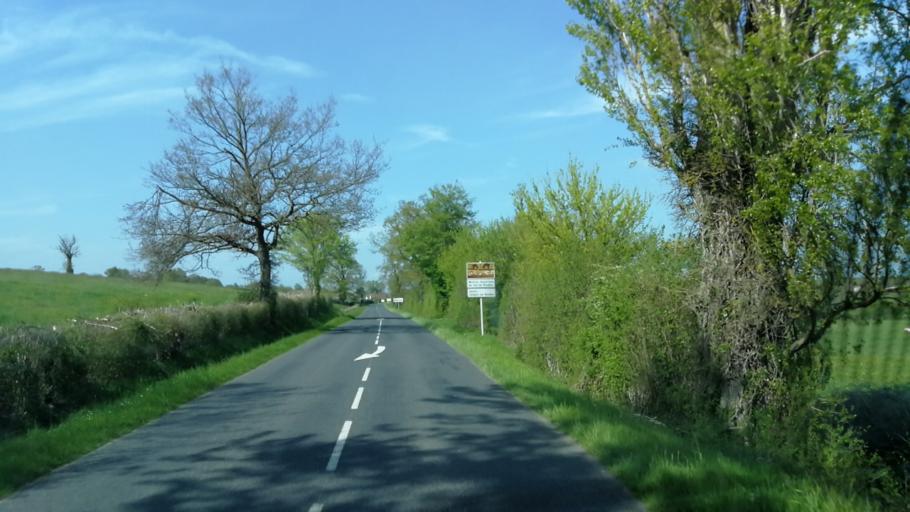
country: FR
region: Auvergne
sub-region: Departement de l'Allier
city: Saint-Gerand-le-Puy
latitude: 46.3646
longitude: 3.5790
